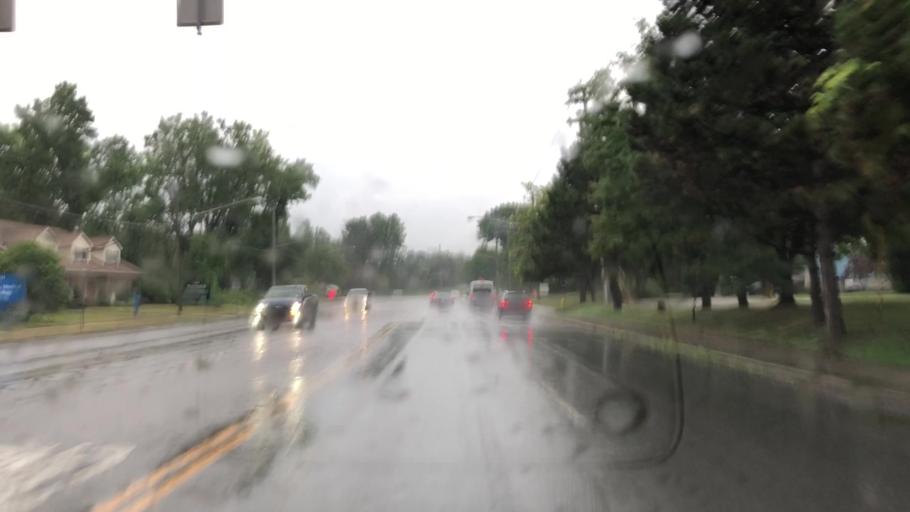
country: US
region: New York
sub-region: Erie County
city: Cheektowaga
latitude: 42.8849
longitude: -78.7558
